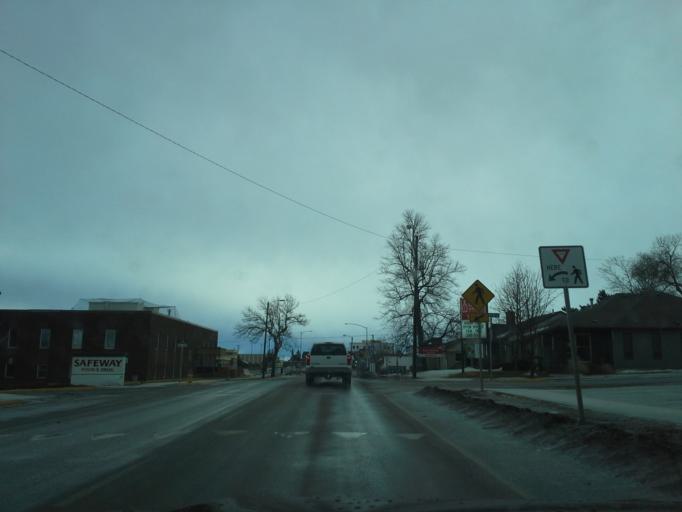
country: US
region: Montana
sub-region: Lewis and Clark County
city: Helena
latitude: 46.5897
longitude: -112.0190
